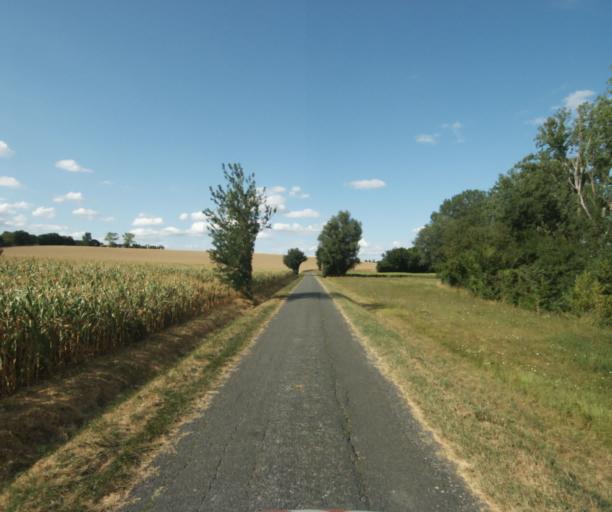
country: FR
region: Midi-Pyrenees
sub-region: Departement du Tarn
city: Puylaurens
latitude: 43.5217
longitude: 1.9910
